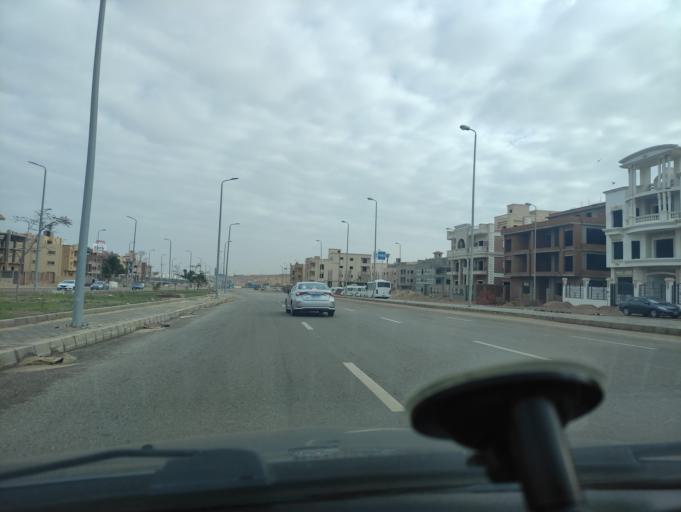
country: EG
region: Muhafazat al Qalyubiyah
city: Al Khankah
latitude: 30.0484
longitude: 31.5291
